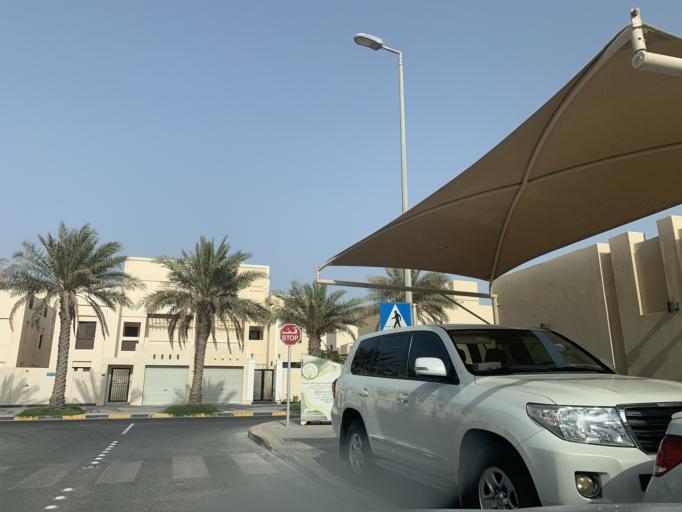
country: BH
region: Manama
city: Jidd Hafs
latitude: 26.2265
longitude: 50.4415
